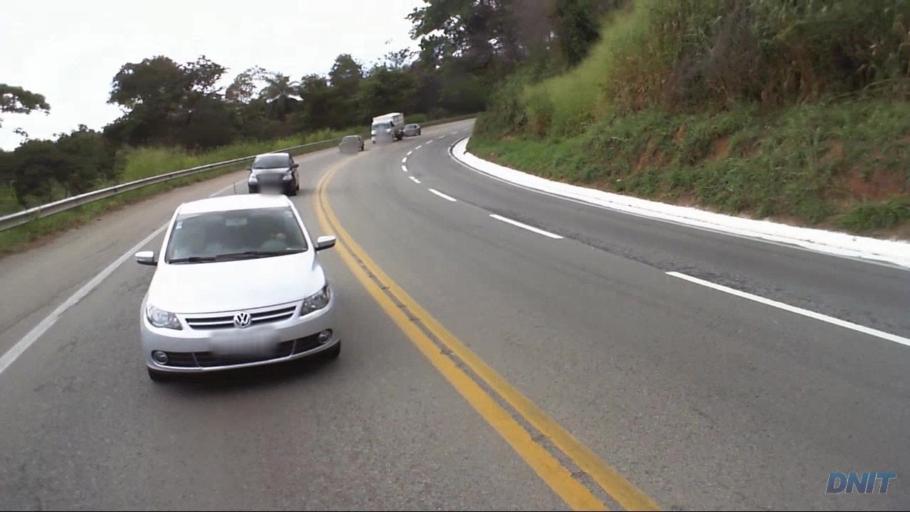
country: BR
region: Minas Gerais
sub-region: Santa Luzia
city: Santa Luzia
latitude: -19.7878
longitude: -43.7435
